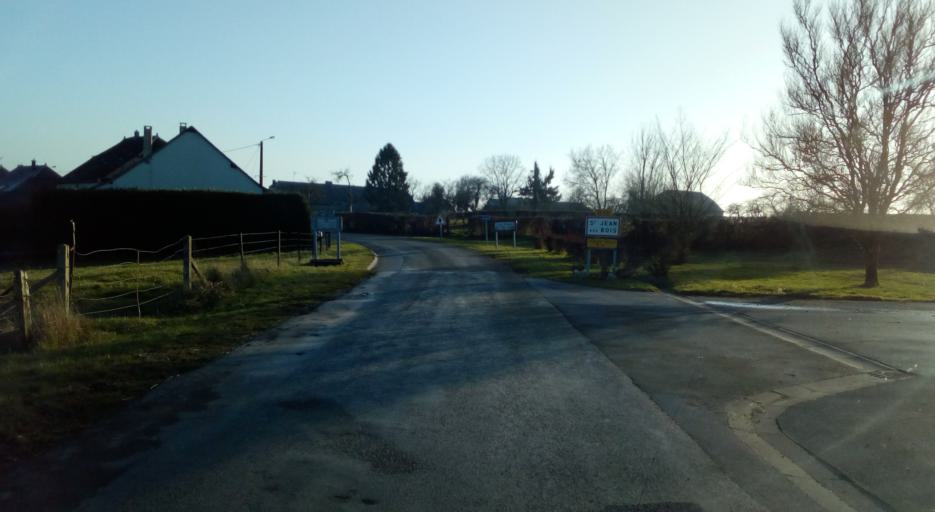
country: FR
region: Picardie
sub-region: Departement de l'Aisne
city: Rozoy-sur-Serre
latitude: 49.7270
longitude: 4.3036
